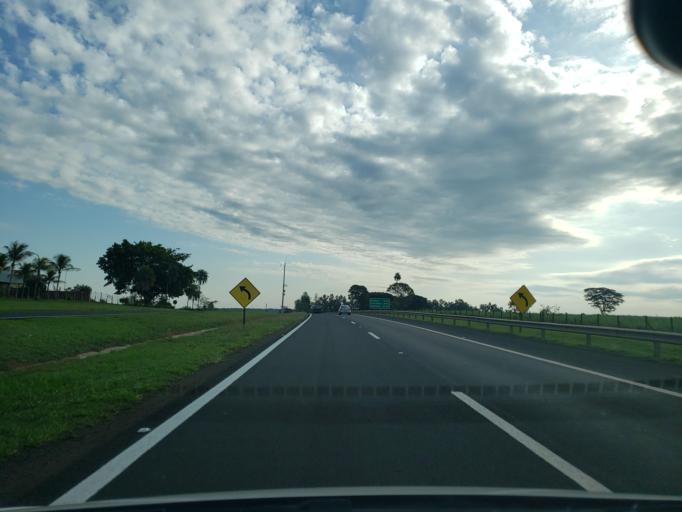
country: BR
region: Sao Paulo
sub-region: Guararapes
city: Guararapes
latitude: -21.2087
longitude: -50.6626
